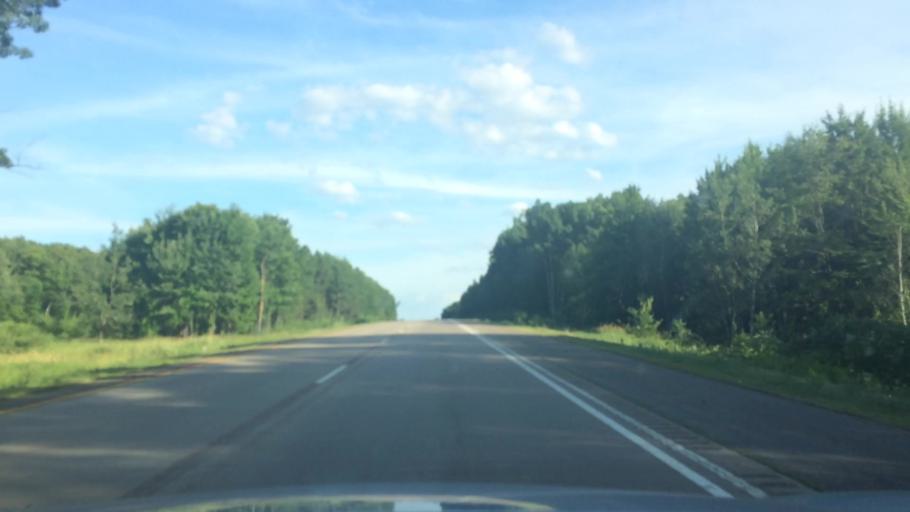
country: US
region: Wisconsin
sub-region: Marathon County
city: Mosinee
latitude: 44.7072
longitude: -89.6558
